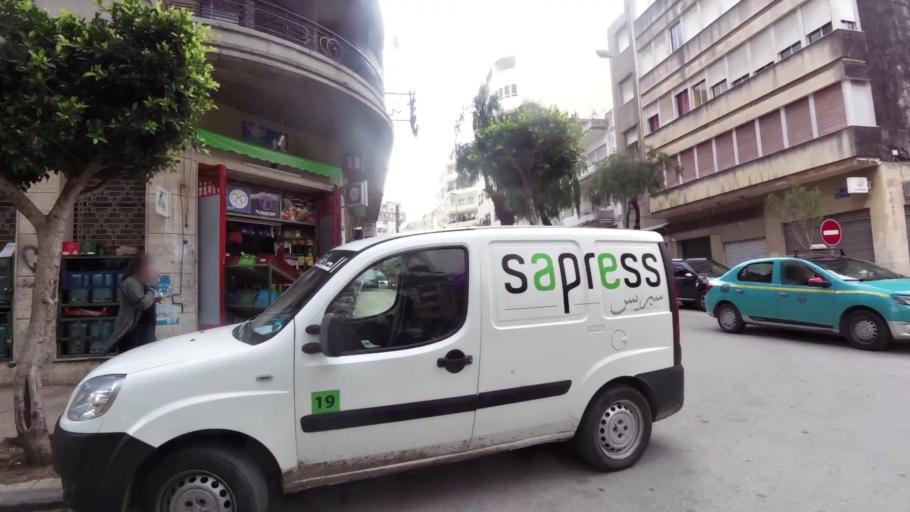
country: MA
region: Tanger-Tetouan
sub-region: Tanger-Assilah
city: Tangier
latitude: 35.7739
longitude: -5.8125
